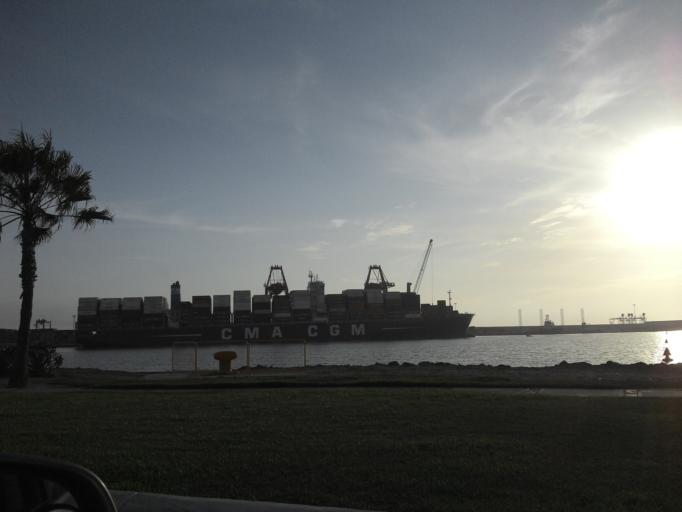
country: MX
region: Baja California
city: Ensenada
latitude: 31.8547
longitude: -116.6249
